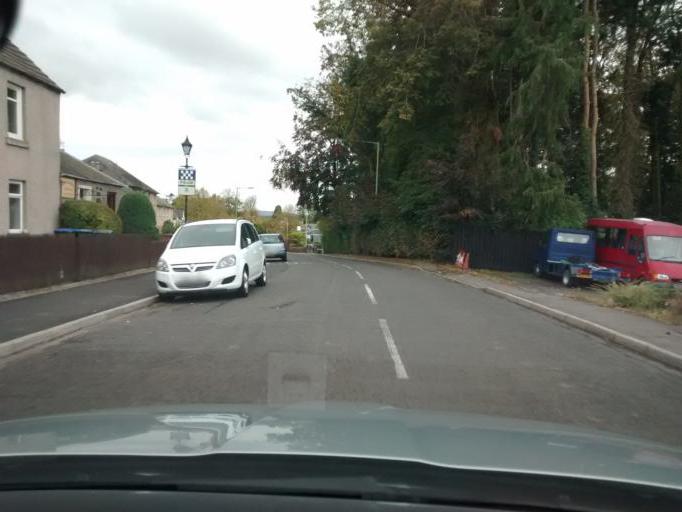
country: GB
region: Scotland
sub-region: Perth and Kinross
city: Stanley
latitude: 56.4821
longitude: -3.4507
